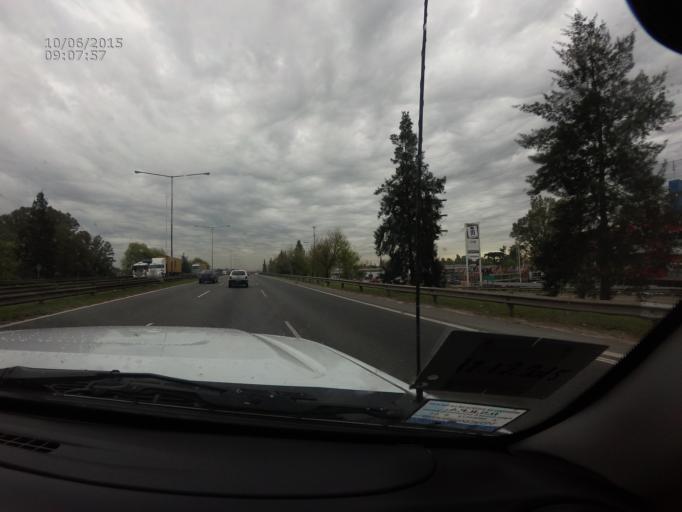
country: AR
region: Buenos Aires
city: Santa Catalina - Dique Lujan
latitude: -34.3961
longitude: -58.7394
